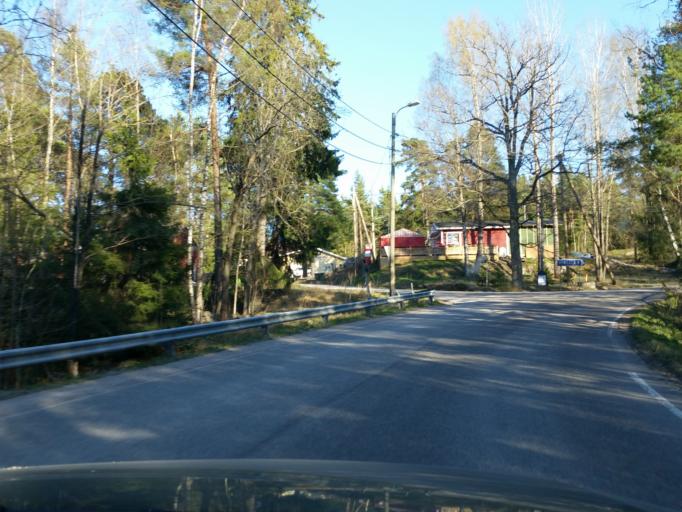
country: FI
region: Uusimaa
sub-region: Helsinki
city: Kirkkonummi
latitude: 60.1007
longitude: 24.5655
